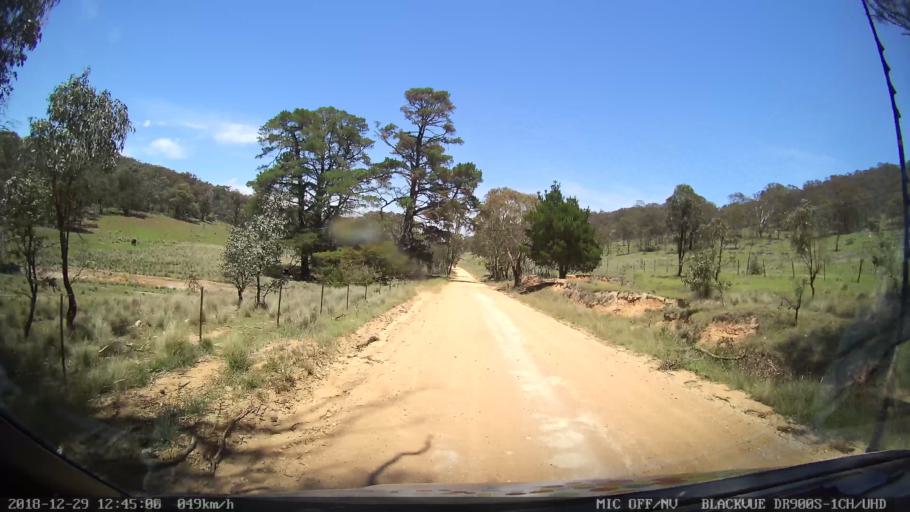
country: AU
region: Australian Capital Territory
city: Macarthur
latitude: -35.6316
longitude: 149.2155
